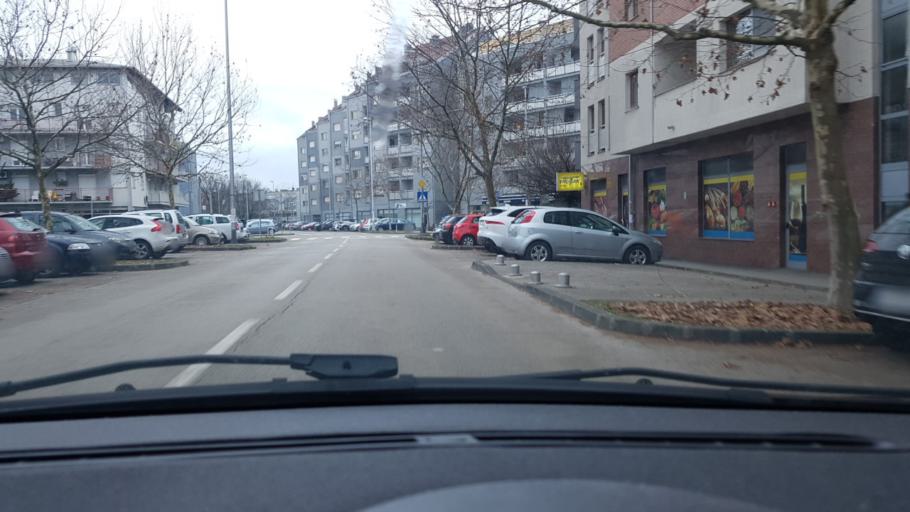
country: HR
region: Grad Zagreb
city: Dubrava
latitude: 45.8167
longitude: 16.0289
